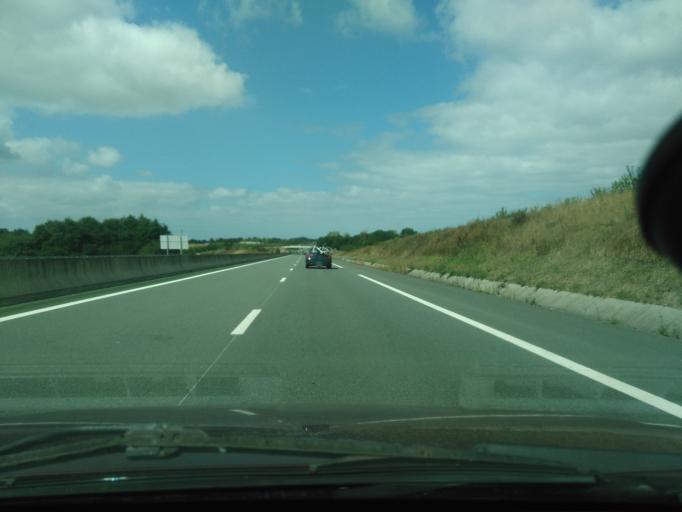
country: FR
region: Pays de la Loire
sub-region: Departement de la Vendee
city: Aubigny
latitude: 46.6296
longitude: -1.4525
